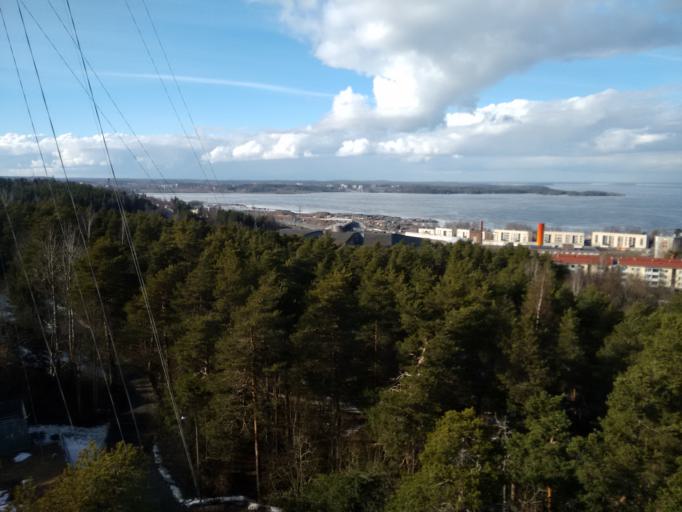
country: FI
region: Pirkanmaa
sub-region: Tampere
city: Tampere
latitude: 61.5020
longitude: 23.7272
